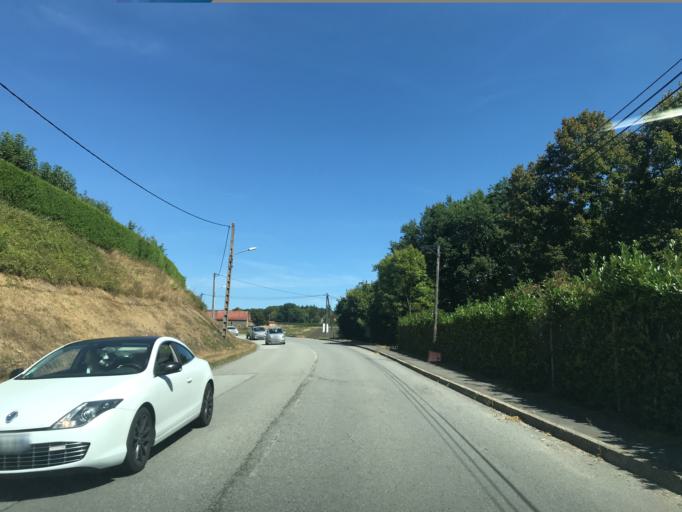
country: FR
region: Limousin
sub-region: Departement de la Creuse
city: Felletin
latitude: 45.8901
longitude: 2.1809
